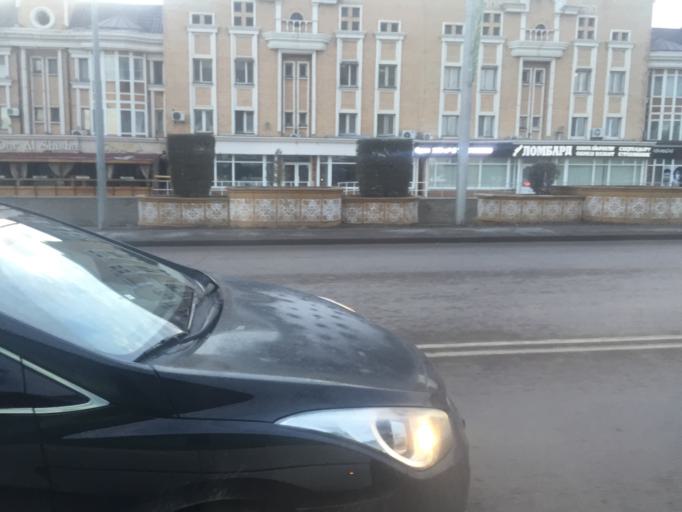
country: KZ
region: Astana Qalasy
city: Astana
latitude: 51.1396
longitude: 71.4177
